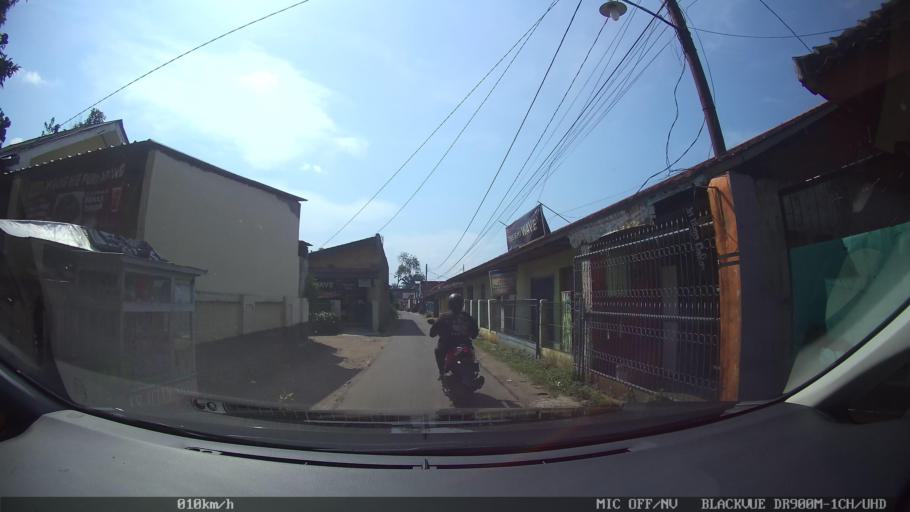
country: ID
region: Lampung
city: Kedaton
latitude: -5.3610
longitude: 105.2437
